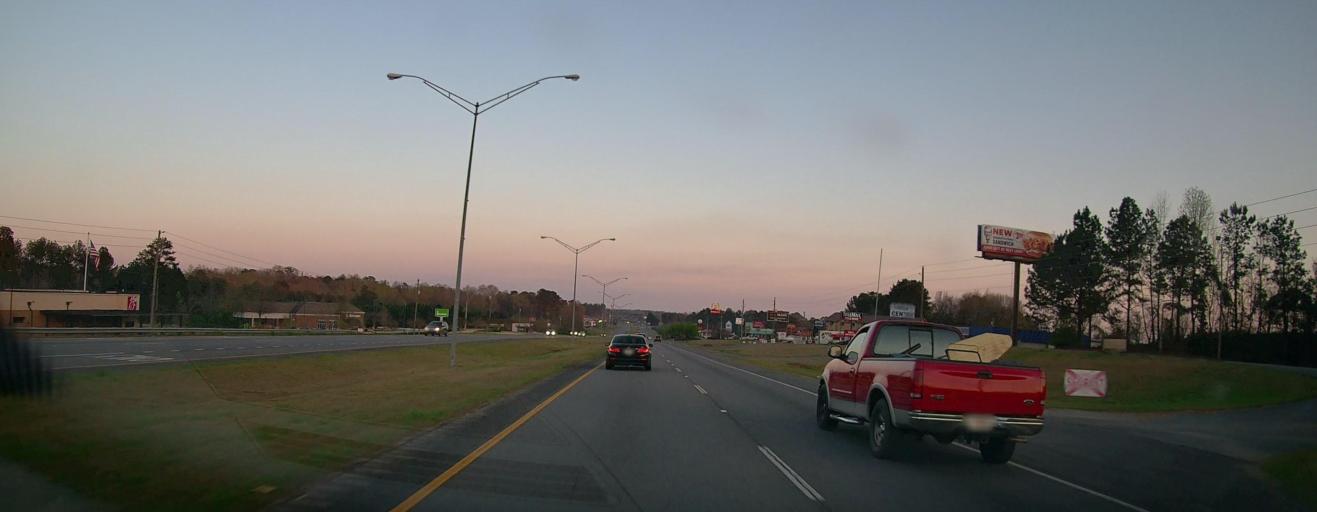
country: US
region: Alabama
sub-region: Tallapoosa County
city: Alexander City
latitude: 32.9259
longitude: -85.9628
